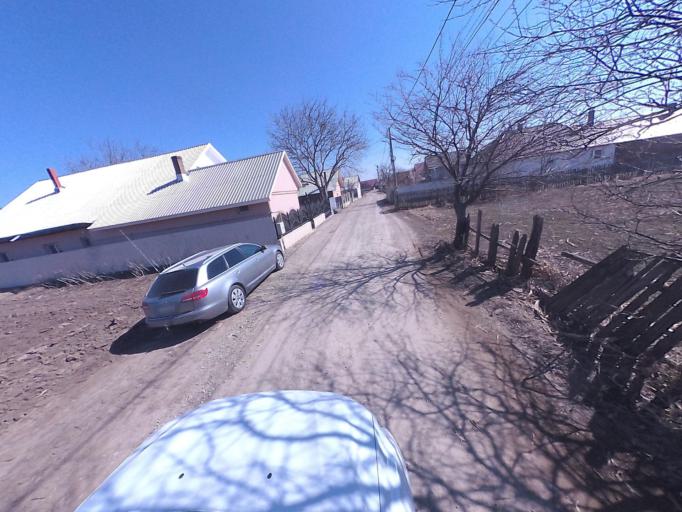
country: RO
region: Neamt
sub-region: Oras Targu Neamt
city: Humulesti
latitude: 47.1933
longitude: 26.3513
